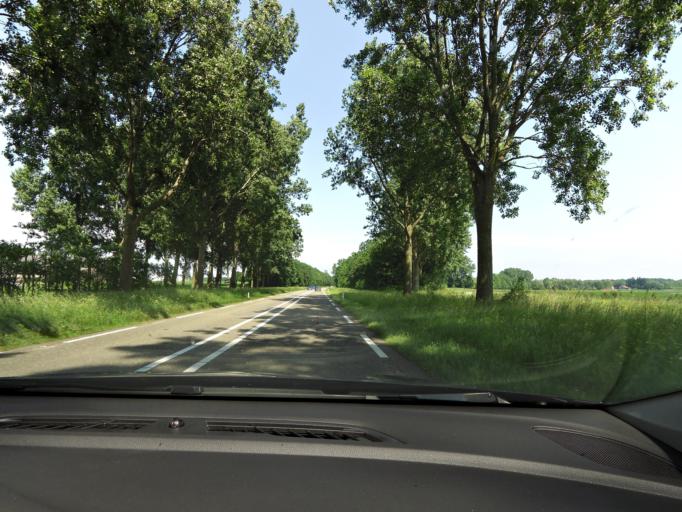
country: NL
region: North Brabant
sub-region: Gemeente Bergen op Zoom
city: Halsteren
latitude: 51.5377
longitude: 4.2572
